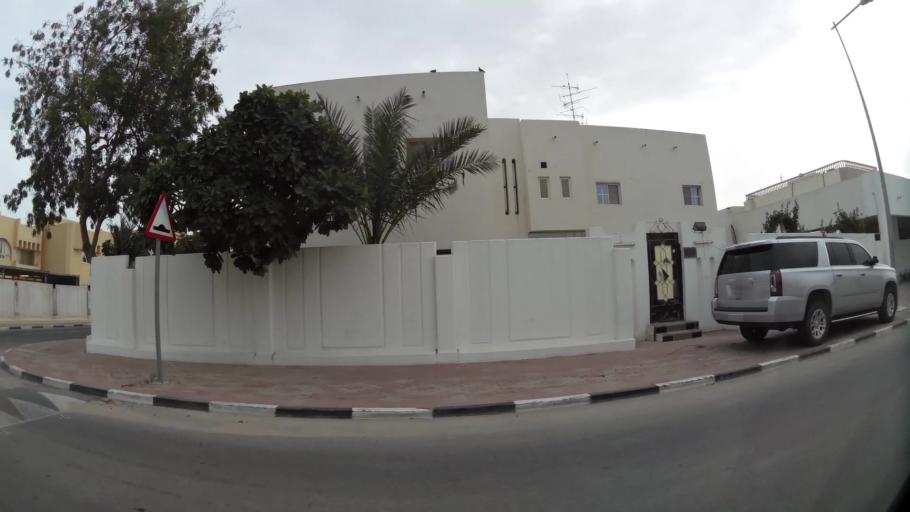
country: QA
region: Baladiyat ad Dawhah
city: Doha
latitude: 25.3349
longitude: 51.5096
